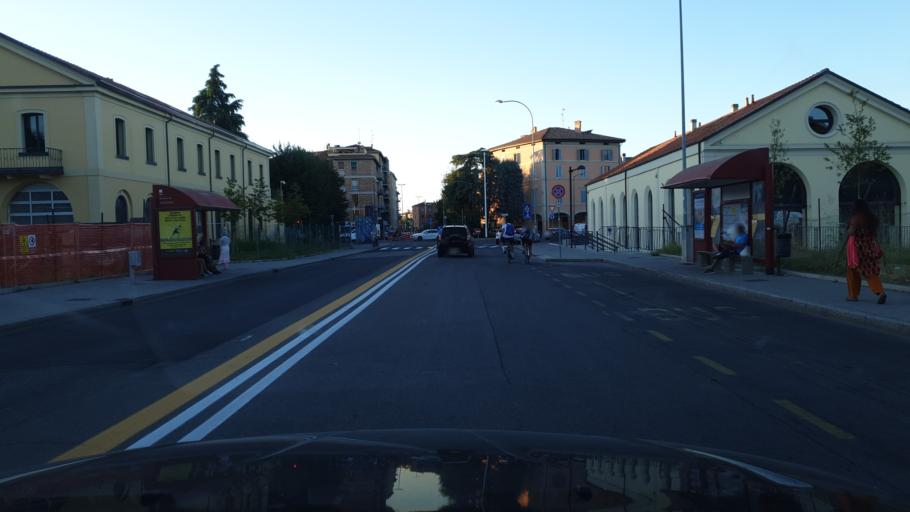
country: IT
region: Emilia-Romagna
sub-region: Provincia di Bologna
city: Bologna
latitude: 44.4989
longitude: 11.3596
